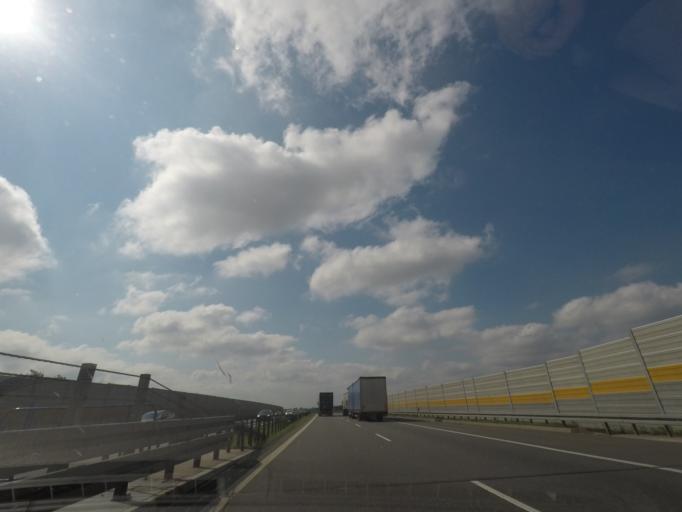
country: PL
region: Kujawsko-Pomorskie
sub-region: Powiat torunski
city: Lubicz Dolny
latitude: 53.1301
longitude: 18.7391
